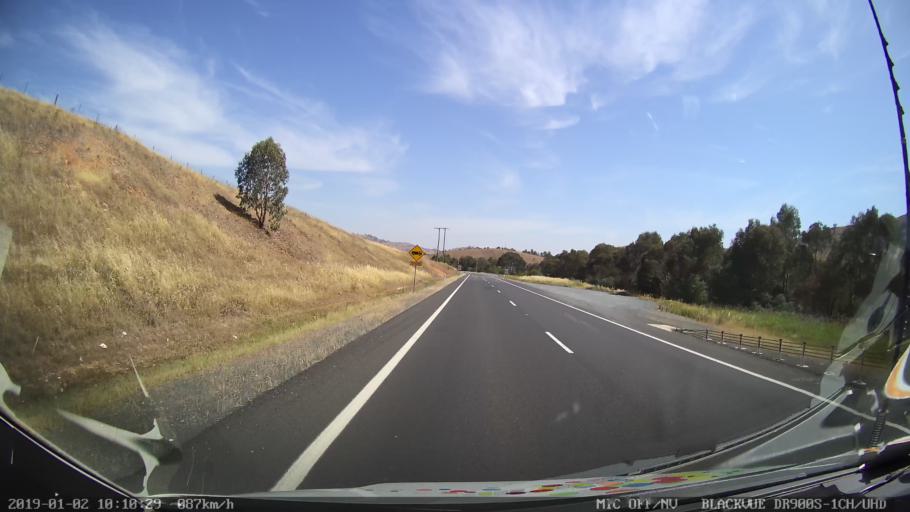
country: AU
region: New South Wales
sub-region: Gundagai
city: Gundagai
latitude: -35.1032
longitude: 148.0963
